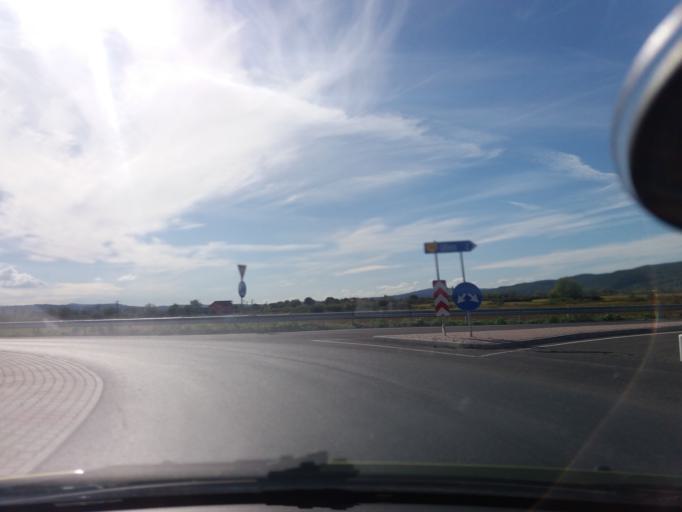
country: RO
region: Hunedoara
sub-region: Comuna Ilia
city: Ilia
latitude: 45.9449
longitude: 22.6230
